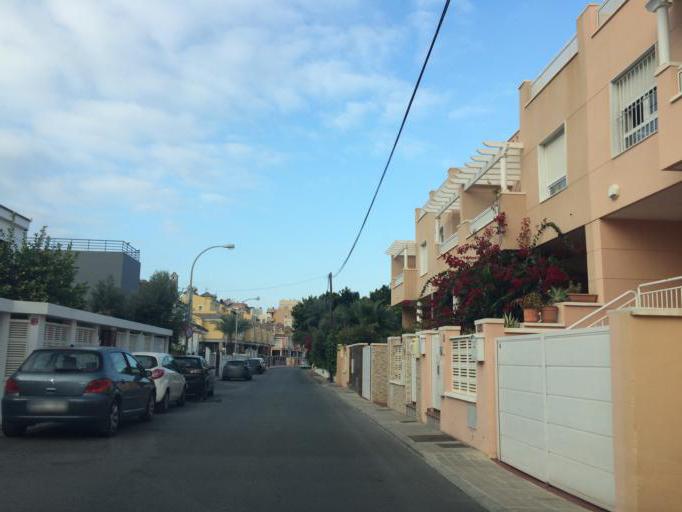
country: ES
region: Andalusia
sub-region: Provincia de Almeria
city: Almeria
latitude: 36.8236
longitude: -2.4363
